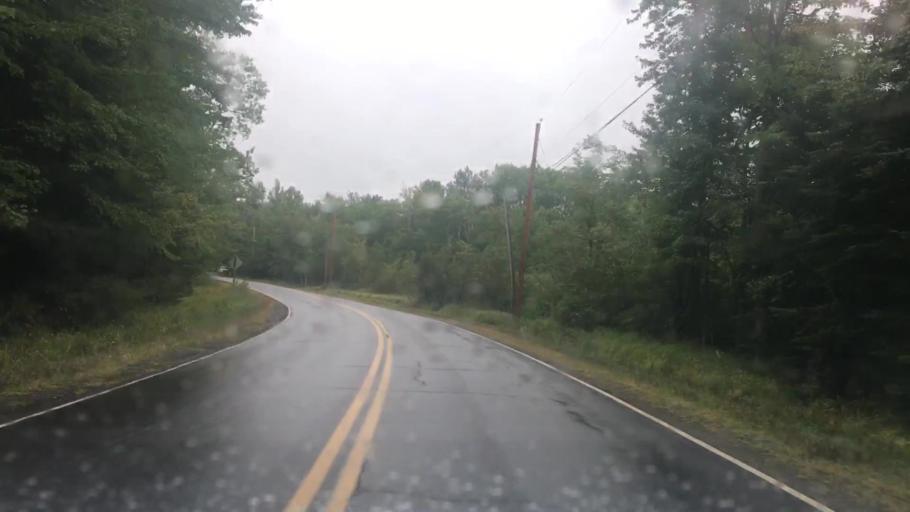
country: US
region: Maine
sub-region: Penobscot County
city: Hudson
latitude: 44.9865
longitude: -68.7960
